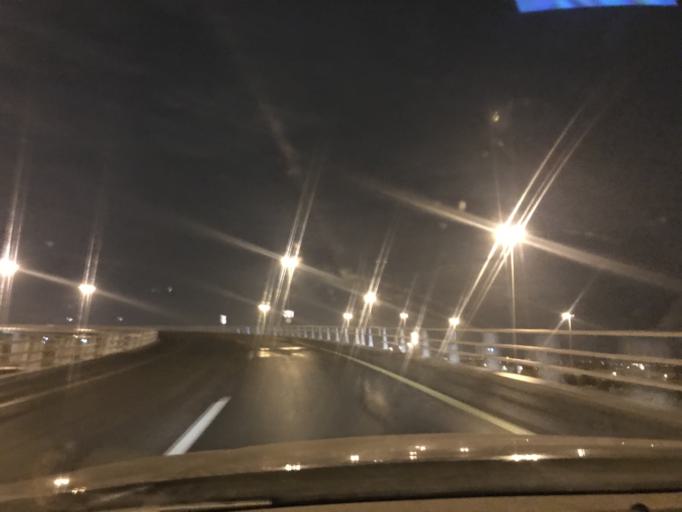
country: SA
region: Ar Riyad
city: Riyadh
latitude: 24.7368
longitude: 46.5892
